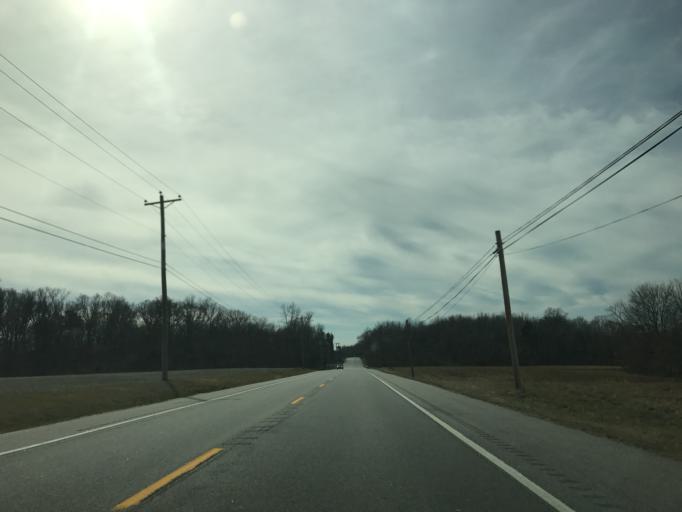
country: US
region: Maryland
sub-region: Queen Anne's County
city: Kingstown
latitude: 39.1252
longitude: -76.0087
